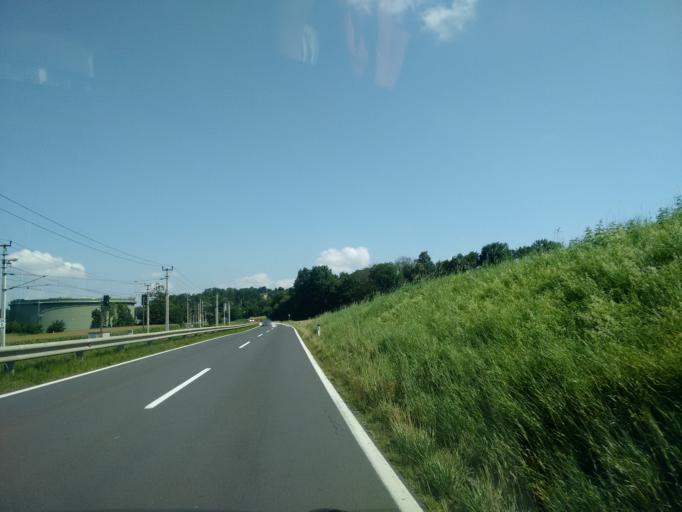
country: AT
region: Upper Austria
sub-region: Politischer Bezirk Kirchdorf an der Krems
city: Kremsmunster
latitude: 48.0173
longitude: 14.1201
